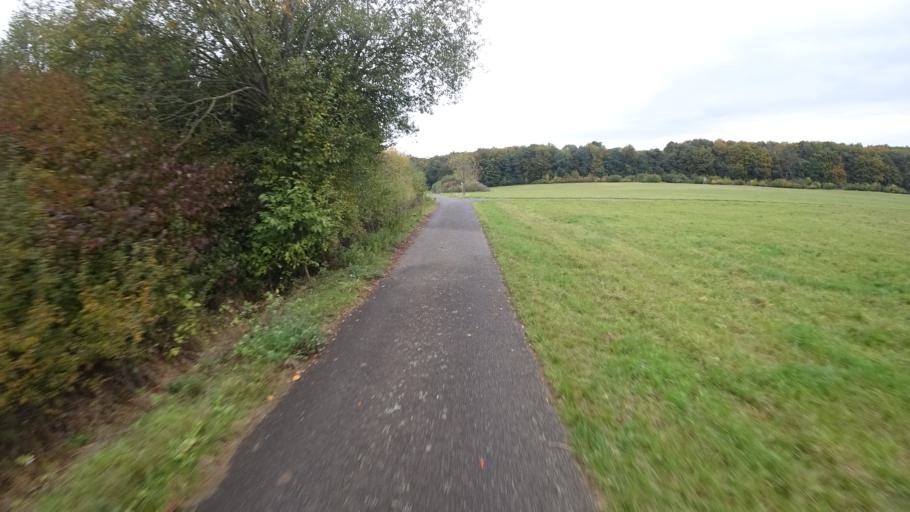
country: DE
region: Rheinland-Pfalz
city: Sessenhausen
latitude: 50.5260
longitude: 7.7244
